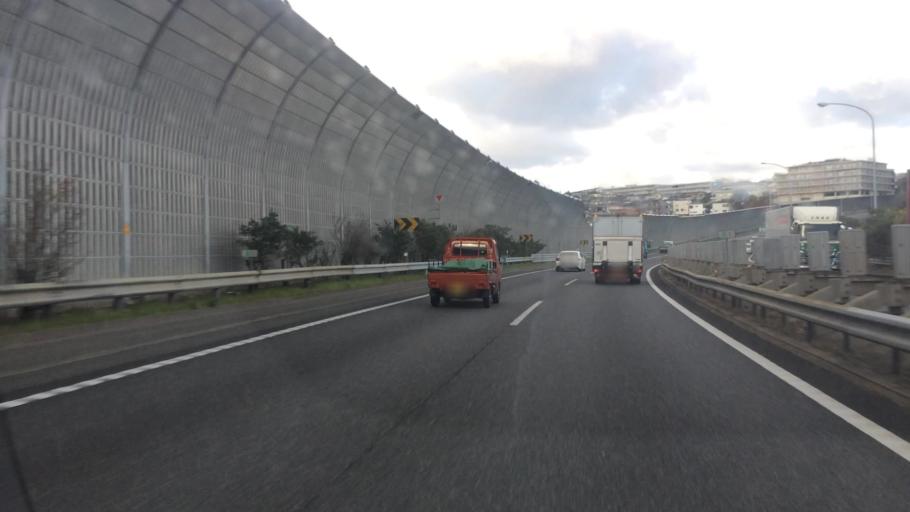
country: JP
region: Hyogo
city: Akashi
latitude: 34.6517
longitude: 135.0396
